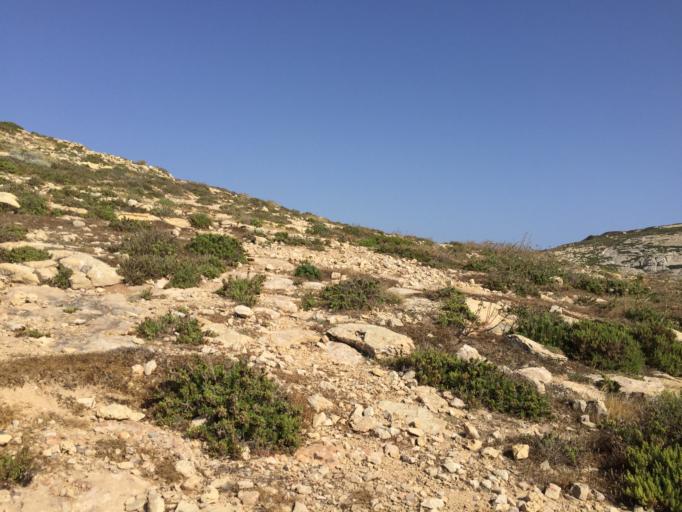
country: MT
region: Saint Lawrence
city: San Lawrenz
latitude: 36.0495
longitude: 14.1912
